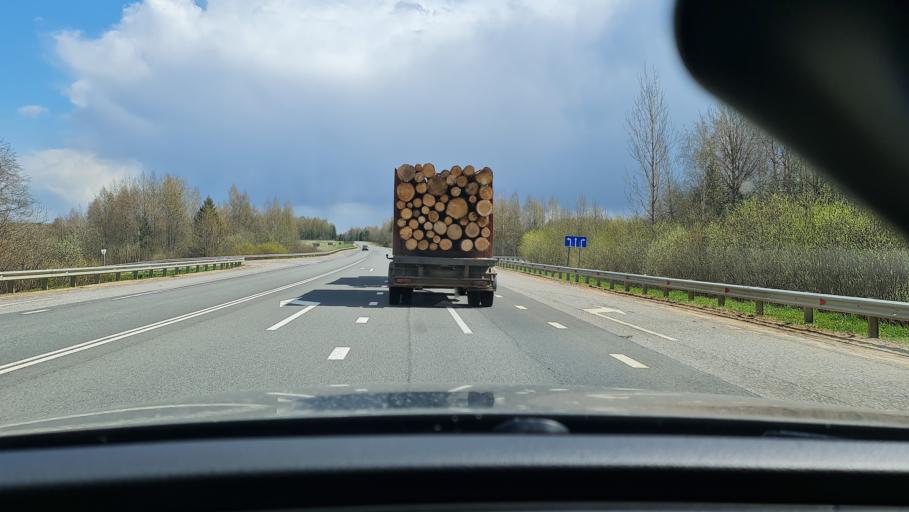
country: RU
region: Tverskaya
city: Zapadnaya Dvina
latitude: 56.3004
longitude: 32.2951
